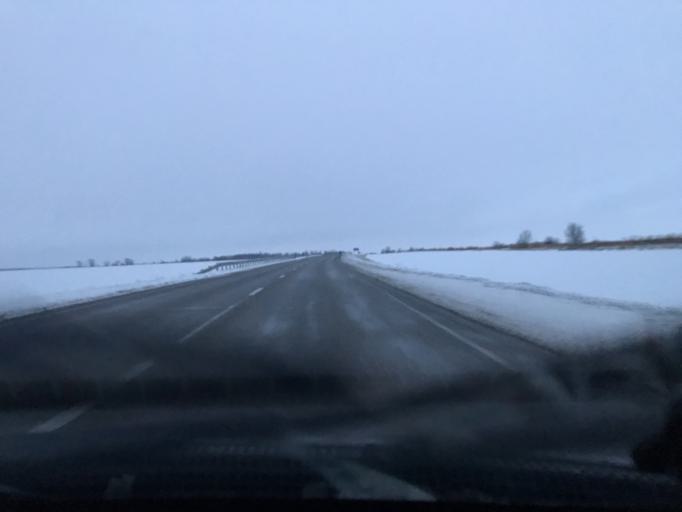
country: RU
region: Rostov
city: Letnik
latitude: 45.9513
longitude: 41.2831
